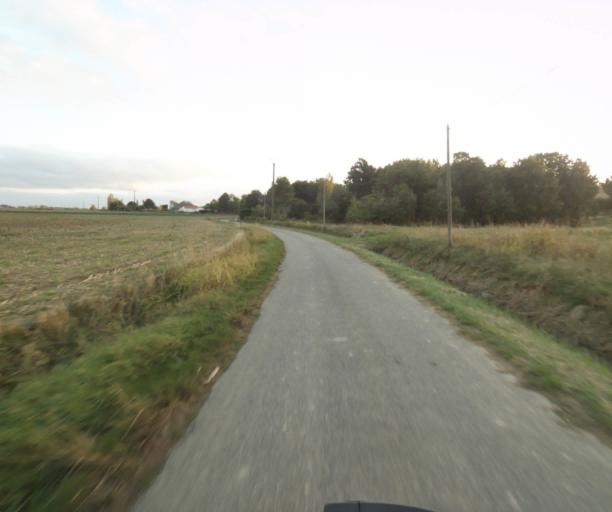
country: FR
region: Midi-Pyrenees
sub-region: Departement du Tarn-et-Garonne
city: Verdun-sur-Garonne
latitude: 43.8262
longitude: 1.2114
